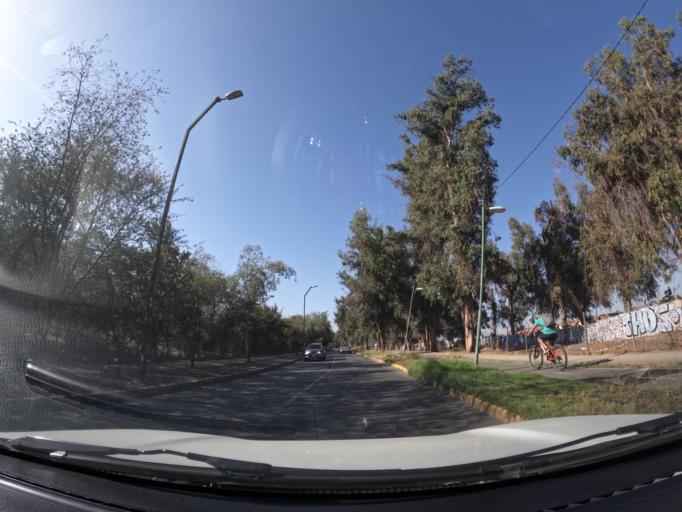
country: CL
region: Santiago Metropolitan
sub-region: Provincia de Santiago
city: Villa Presidente Frei, Nunoa, Santiago, Chile
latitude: -33.5070
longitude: -70.5436
